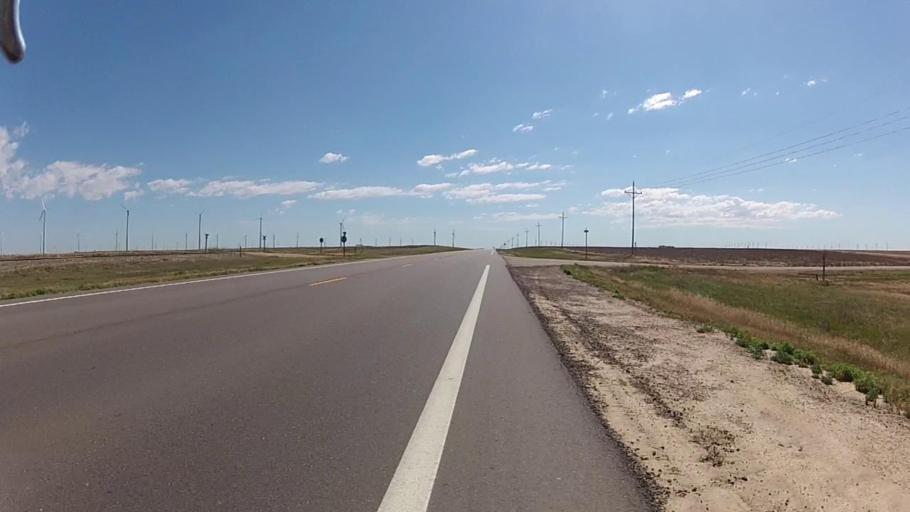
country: US
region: Kansas
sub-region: Gray County
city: Cimarron
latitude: 37.6067
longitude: -100.4165
